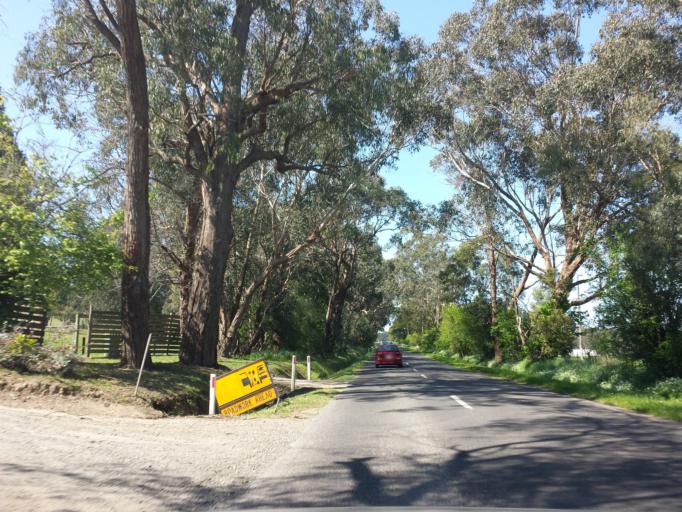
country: AU
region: Victoria
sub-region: Yarra Ranges
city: Woori Yallock
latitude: -37.7866
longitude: 145.4650
